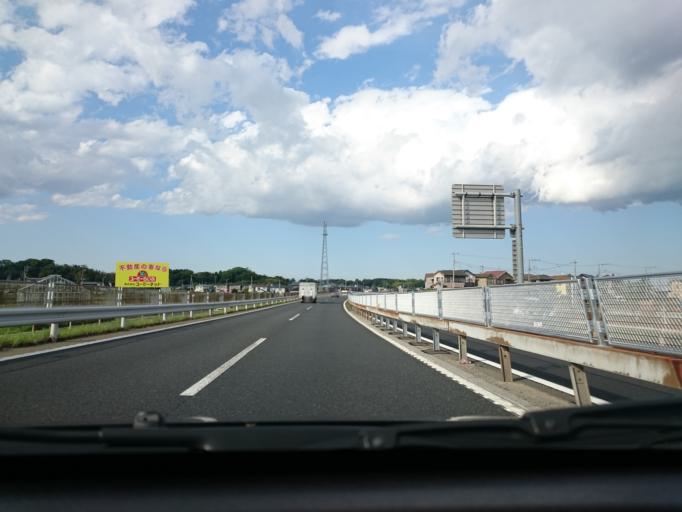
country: JP
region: Kanagawa
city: Isehara
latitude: 35.3709
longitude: 139.3128
